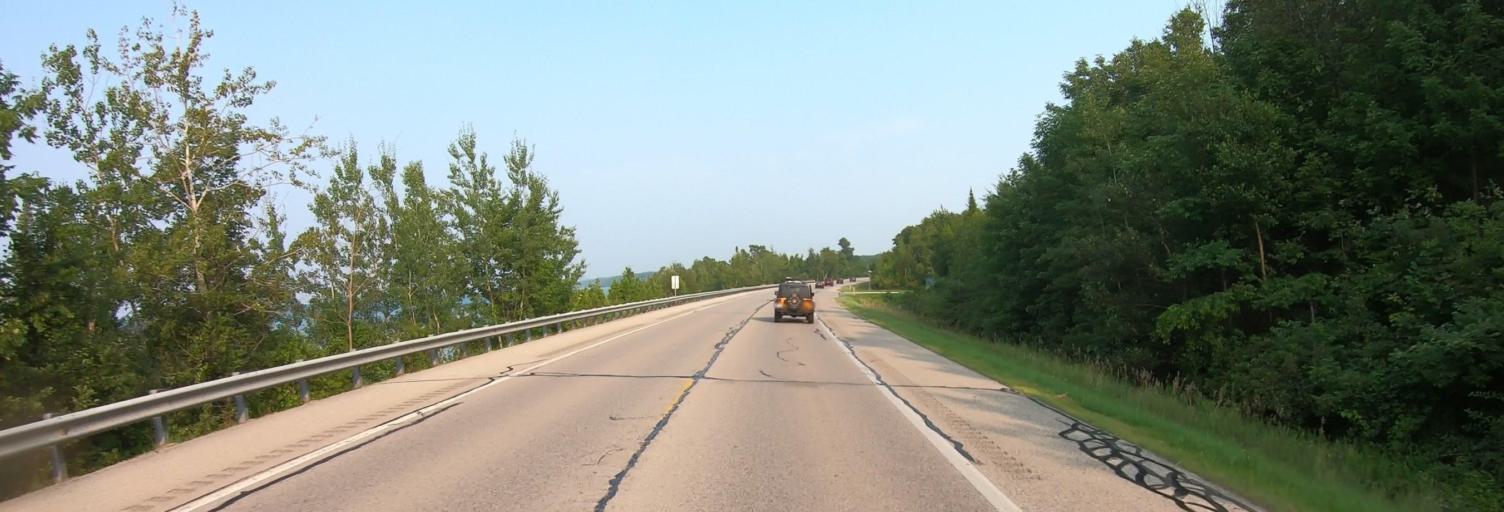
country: US
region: Michigan
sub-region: Charlevoix County
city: Charlevoix
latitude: 45.3676
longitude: -85.1289
